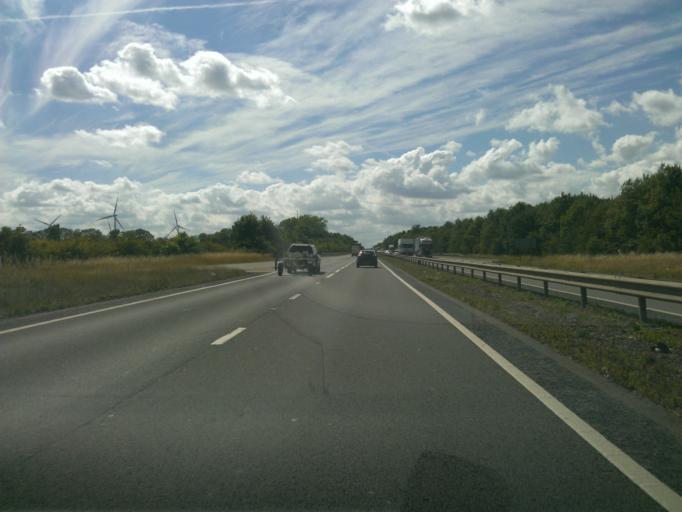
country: GB
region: England
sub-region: Northamptonshire
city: Finedon
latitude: 52.3833
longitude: -0.6245
